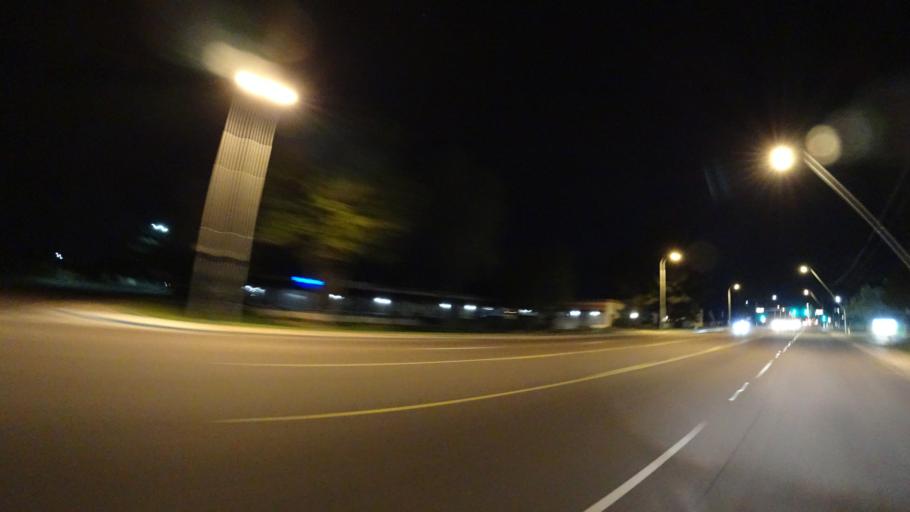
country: US
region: Arizona
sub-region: Maricopa County
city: Chandler
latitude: 33.3207
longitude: -111.8485
